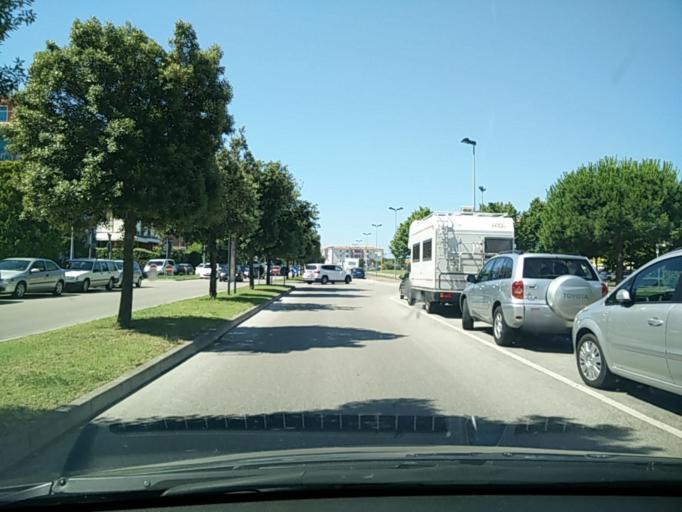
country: IT
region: Veneto
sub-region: Provincia di Venezia
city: Caorle
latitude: 45.6081
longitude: 12.8927
